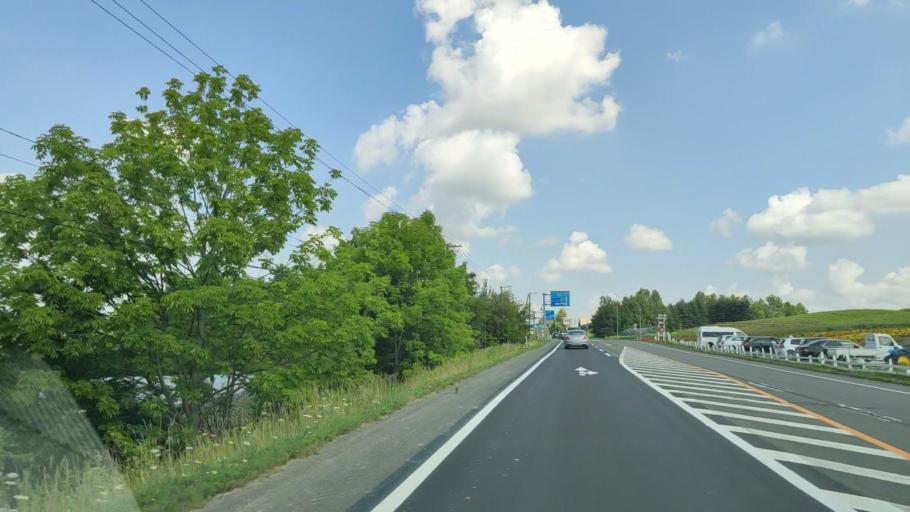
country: JP
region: Hokkaido
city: Shimo-furano
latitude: 43.5420
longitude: 142.4386
